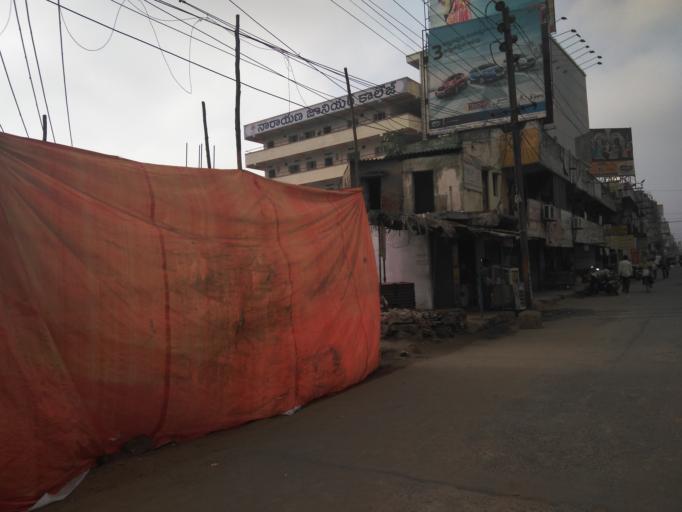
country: IN
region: Andhra Pradesh
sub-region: Nellore
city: Nellore
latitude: 14.4442
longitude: 79.9787
